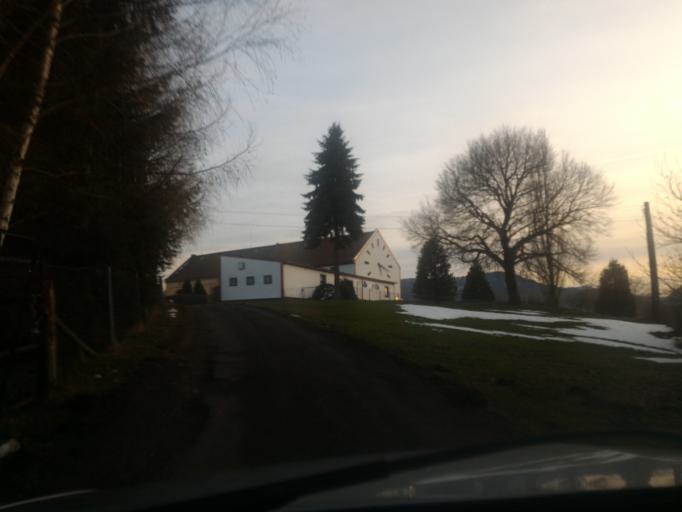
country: DE
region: Saxony
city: Olbersdorf
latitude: 50.8723
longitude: 14.7767
